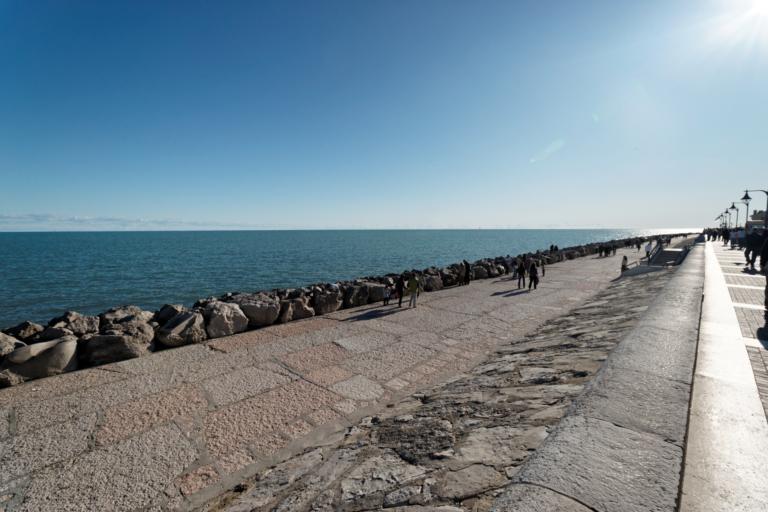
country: IT
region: Veneto
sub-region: Provincia di Venezia
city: Caorle
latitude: 45.5993
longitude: 12.8913
